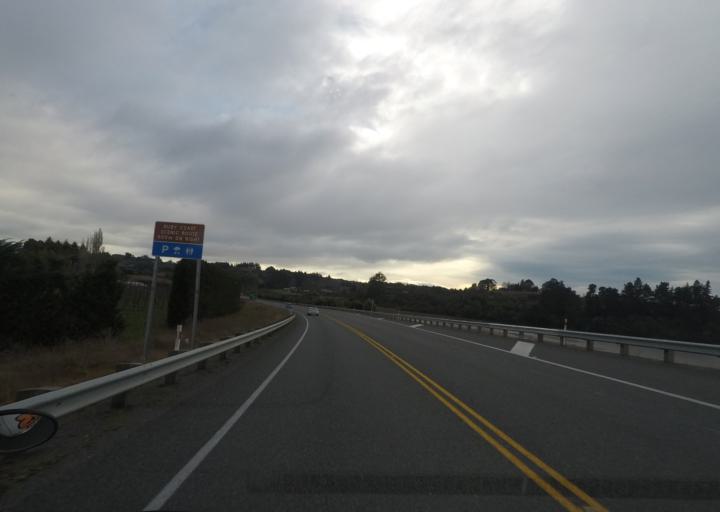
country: NZ
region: Tasman
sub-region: Tasman District
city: Mapua
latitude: -41.2565
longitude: 173.0731
